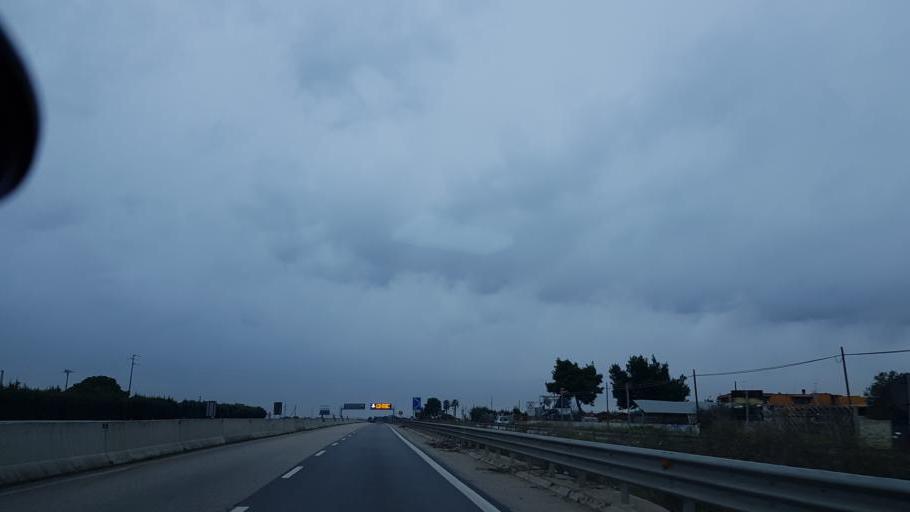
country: IT
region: Apulia
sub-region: Provincia di Brindisi
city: Brindisi
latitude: 40.6162
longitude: 17.9027
